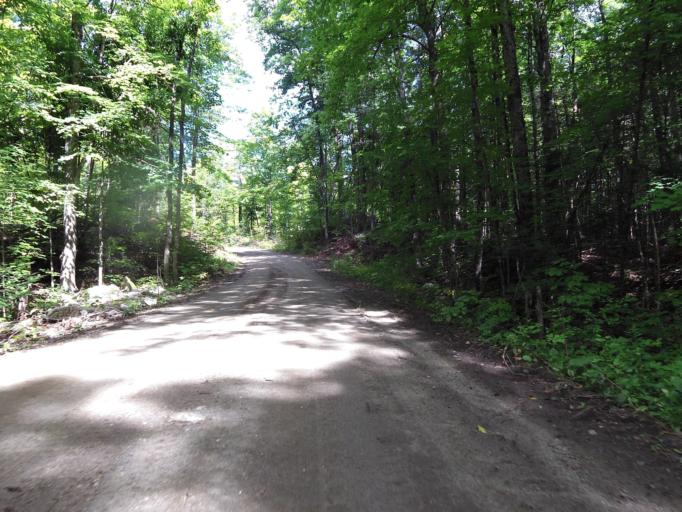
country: CA
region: Ontario
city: Renfrew
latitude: 45.1269
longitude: -76.7191
